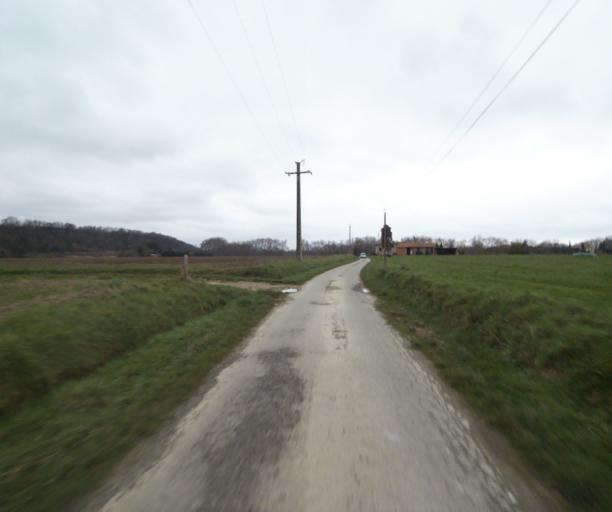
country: FR
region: Midi-Pyrenees
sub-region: Departement de l'Ariege
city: Saverdun
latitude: 43.2152
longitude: 1.5930
